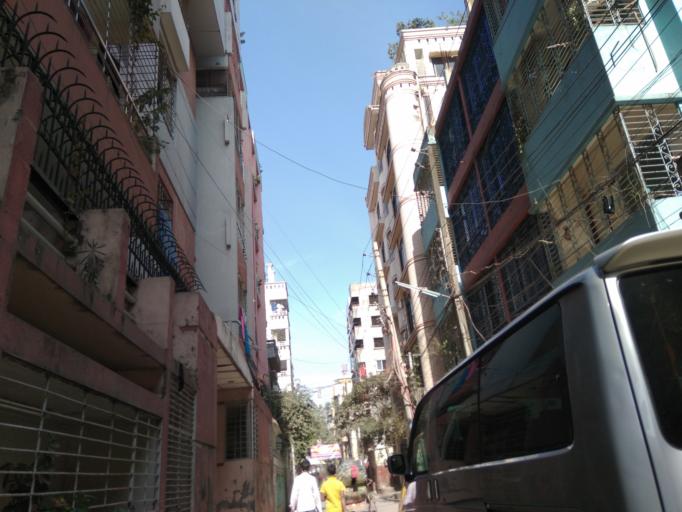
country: BD
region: Dhaka
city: Azimpur
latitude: 23.7736
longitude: 90.3593
